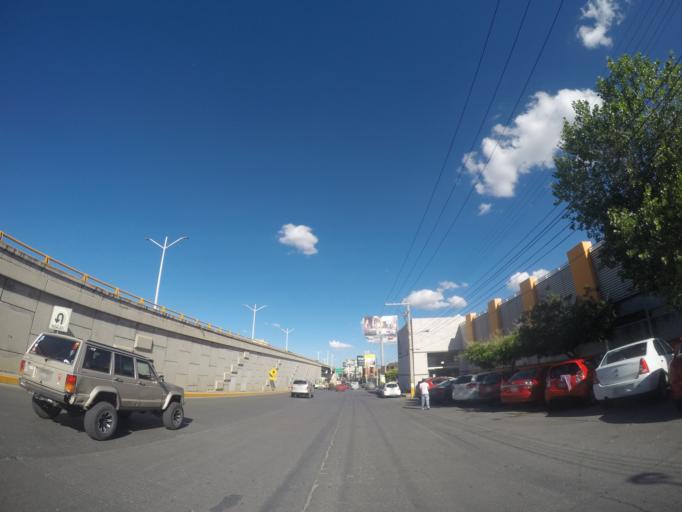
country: MX
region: San Luis Potosi
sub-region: San Luis Potosi
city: San Luis Potosi
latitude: 22.1418
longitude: -101.0151
